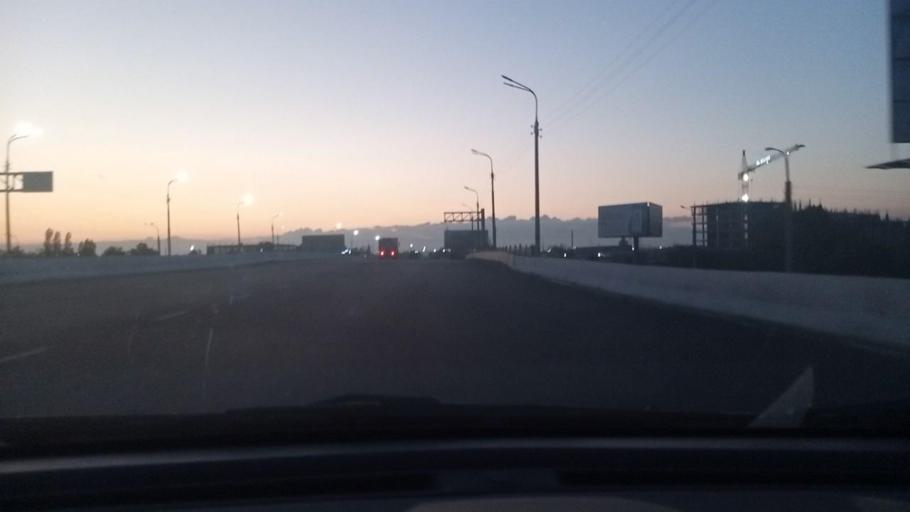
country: UZ
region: Toshkent Shahri
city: Tashkent
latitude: 41.2432
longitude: 69.2165
